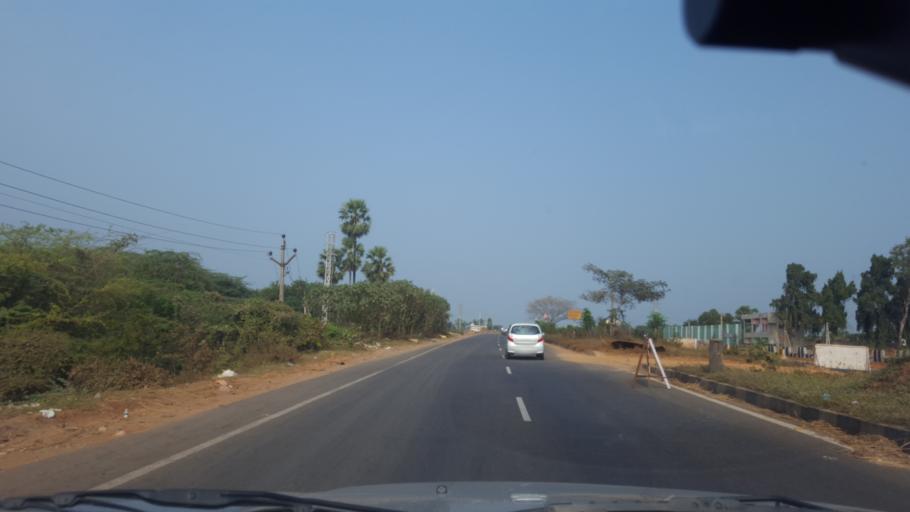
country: IN
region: Andhra Pradesh
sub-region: West Godavari
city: Eluru
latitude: 16.6435
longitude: 80.9880
